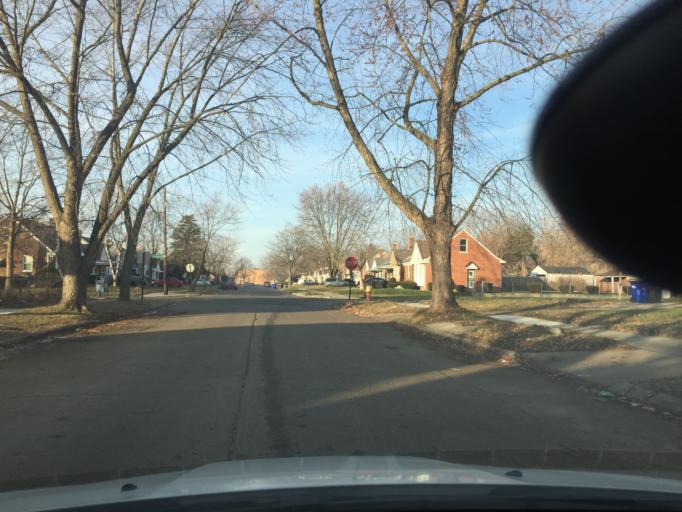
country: US
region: Michigan
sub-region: Macomb County
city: Eastpointe
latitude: 42.4410
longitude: -82.9554
